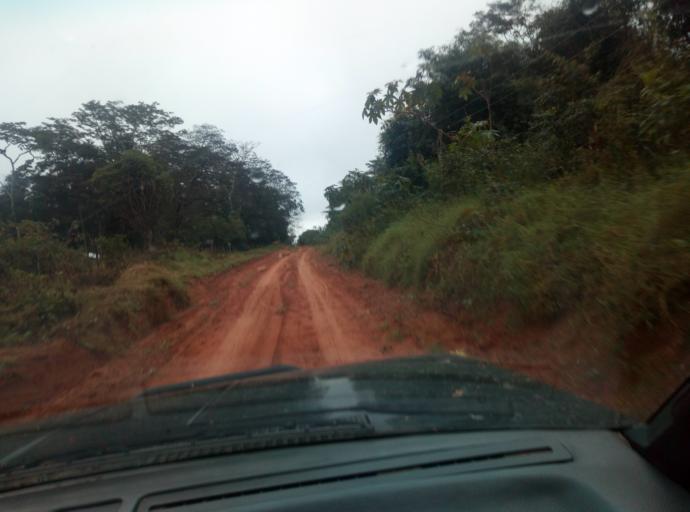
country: PY
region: Caaguazu
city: Carayao
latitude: -25.1919
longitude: -56.3408
